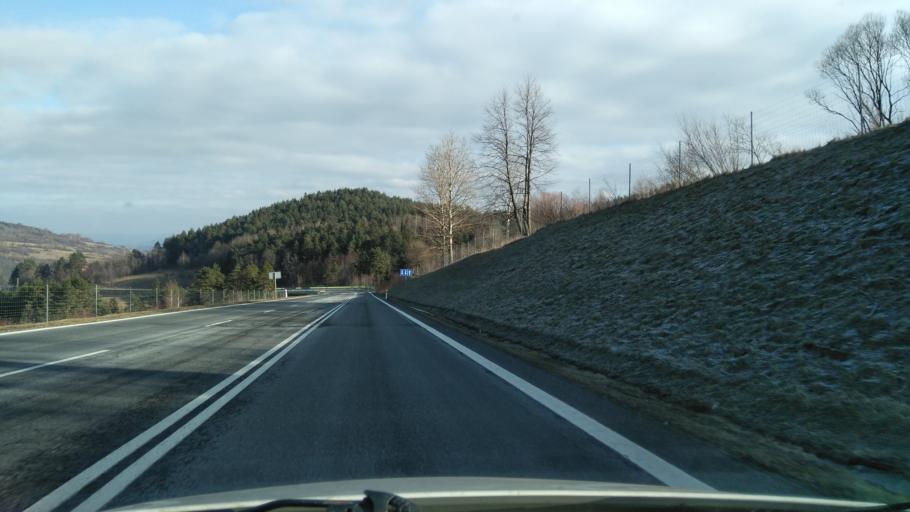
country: PL
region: Silesian Voivodeship
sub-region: Powiat zywiecki
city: Milowka
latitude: 49.5567
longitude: 19.0574
